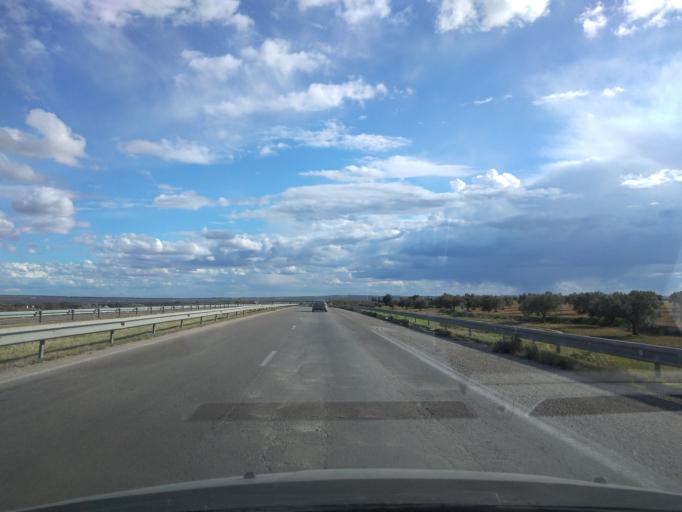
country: TN
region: Al Munastir
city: Manzil Kamil
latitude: 35.6087
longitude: 10.5978
